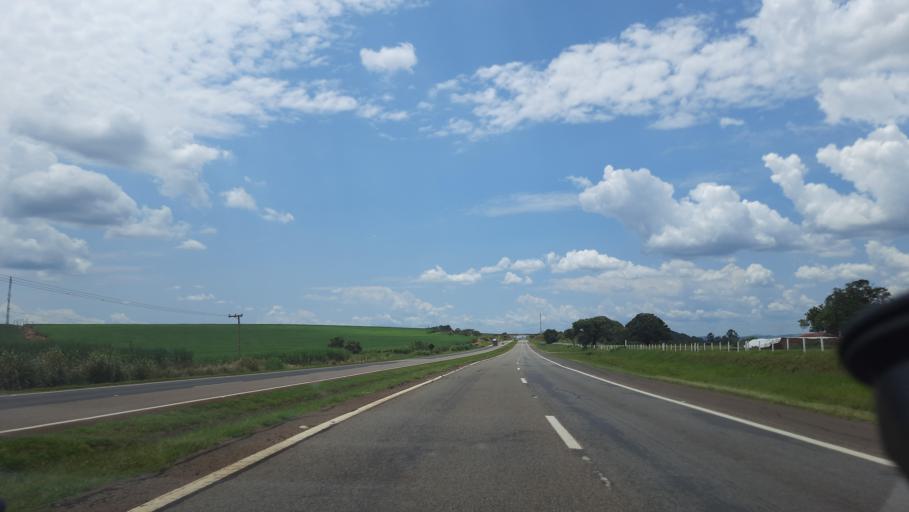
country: BR
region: Sao Paulo
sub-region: Casa Branca
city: Casa Branca
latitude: -21.7013
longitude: -47.0839
